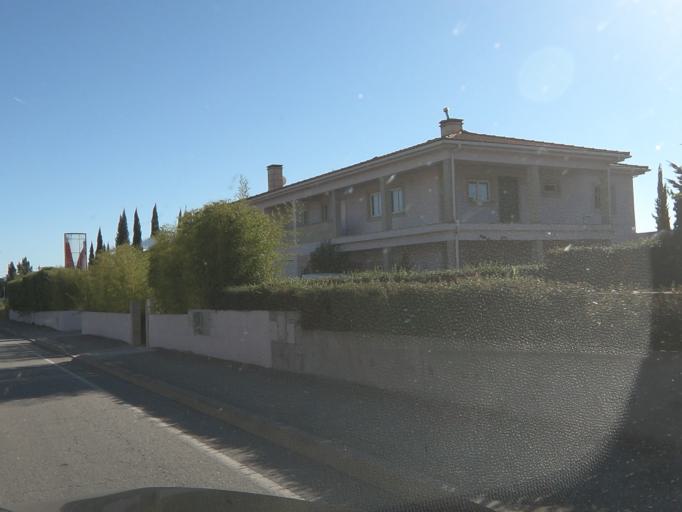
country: PT
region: Vila Real
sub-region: Valpacos
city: Valpacos
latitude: 41.6245
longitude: -7.3123
